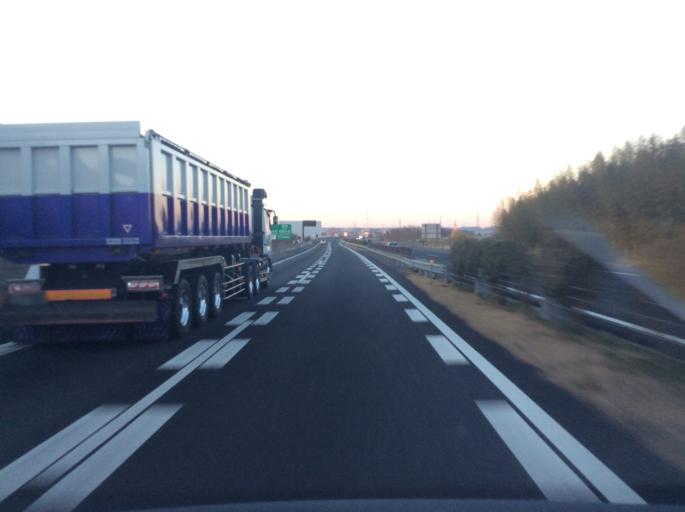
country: JP
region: Ibaraki
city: Funaishikawa
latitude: 36.5163
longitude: 140.5822
